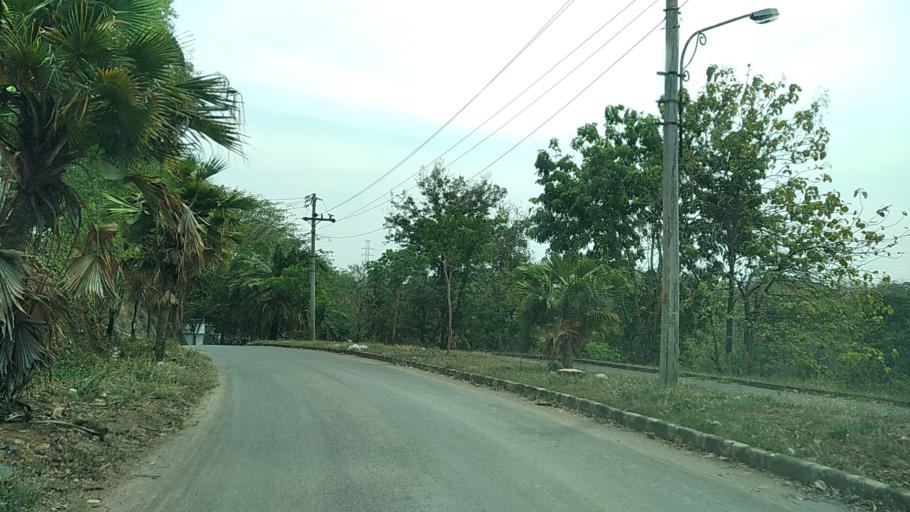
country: ID
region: Central Java
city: Semarang
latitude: -7.0470
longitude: 110.4379
